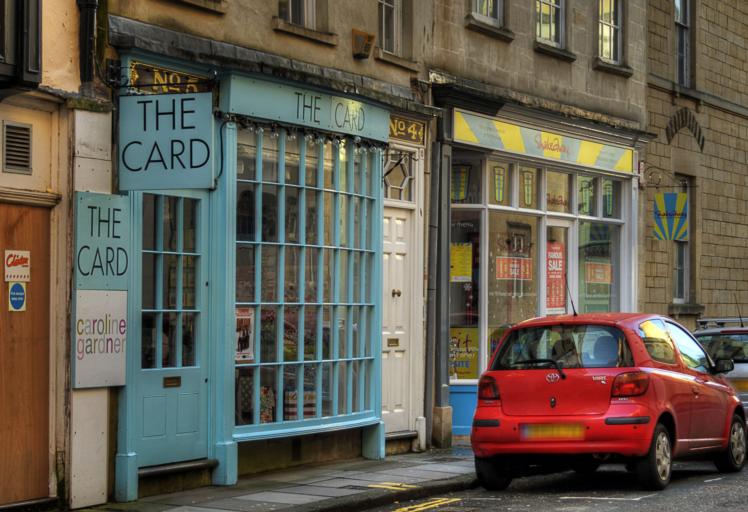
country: GB
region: England
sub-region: Bath and North East Somerset
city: Bath
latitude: 51.3805
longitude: -2.3600
